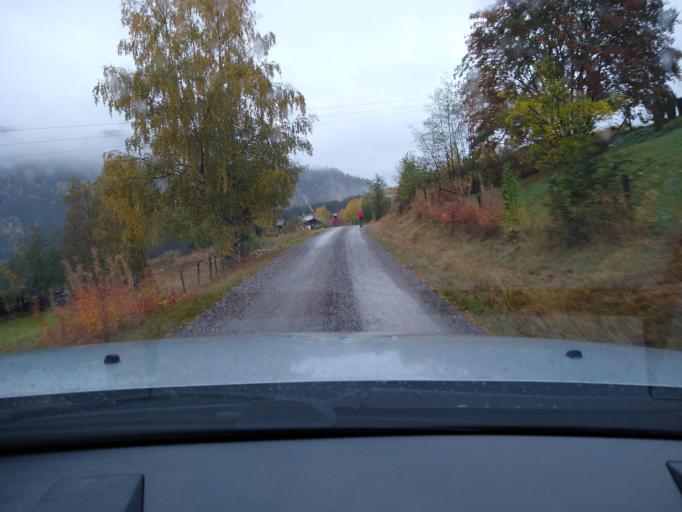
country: NO
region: Oppland
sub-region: Ringebu
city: Ringebu
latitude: 61.5462
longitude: 10.1497
